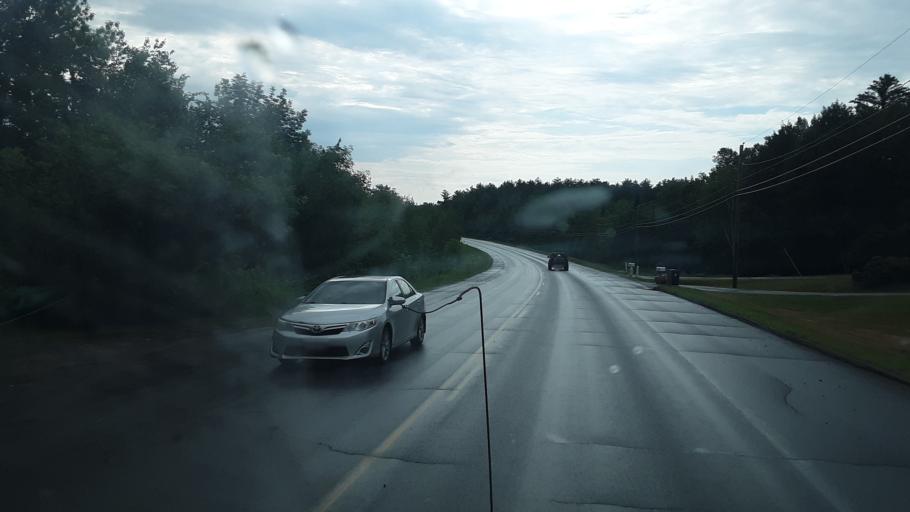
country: US
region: Maine
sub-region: Penobscot County
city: Milford
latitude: 44.9472
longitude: -68.6895
